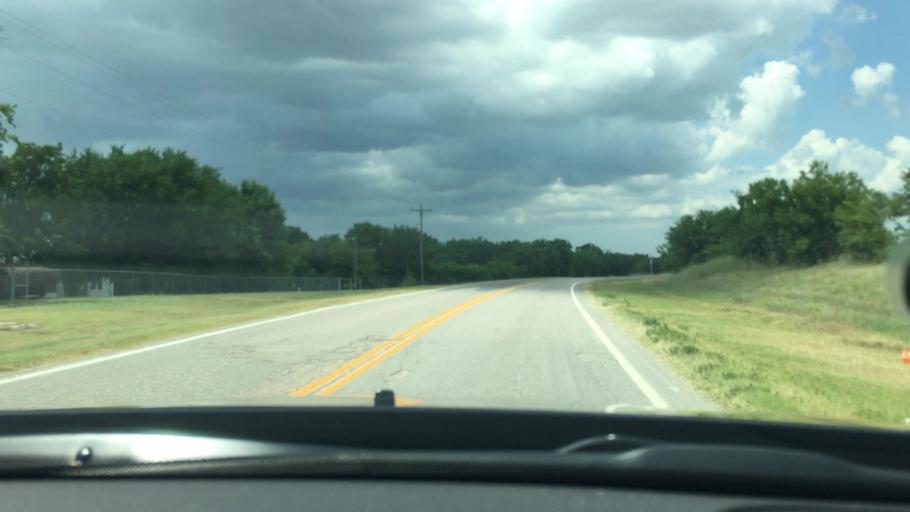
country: US
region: Oklahoma
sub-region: Pontotoc County
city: Ada
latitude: 34.5254
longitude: -96.6342
